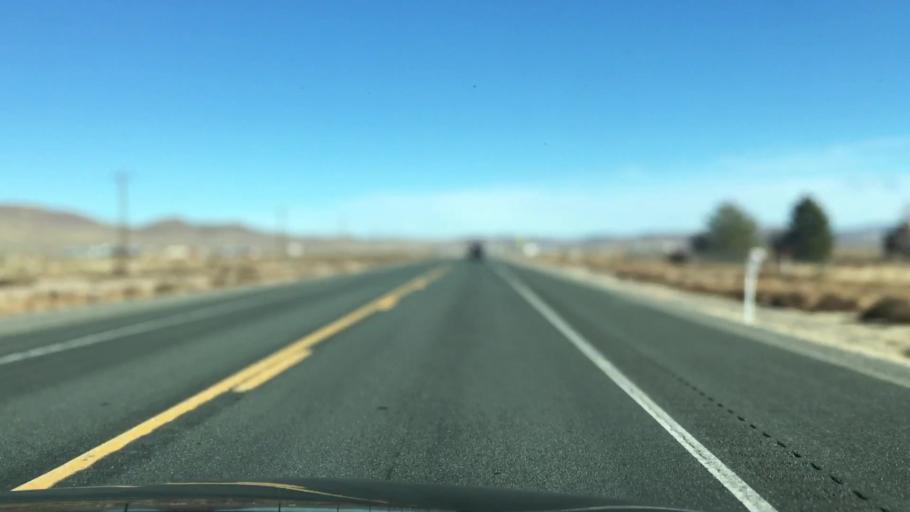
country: US
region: Nevada
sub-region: Lyon County
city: Silver Springs
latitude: 39.3975
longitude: -119.2759
